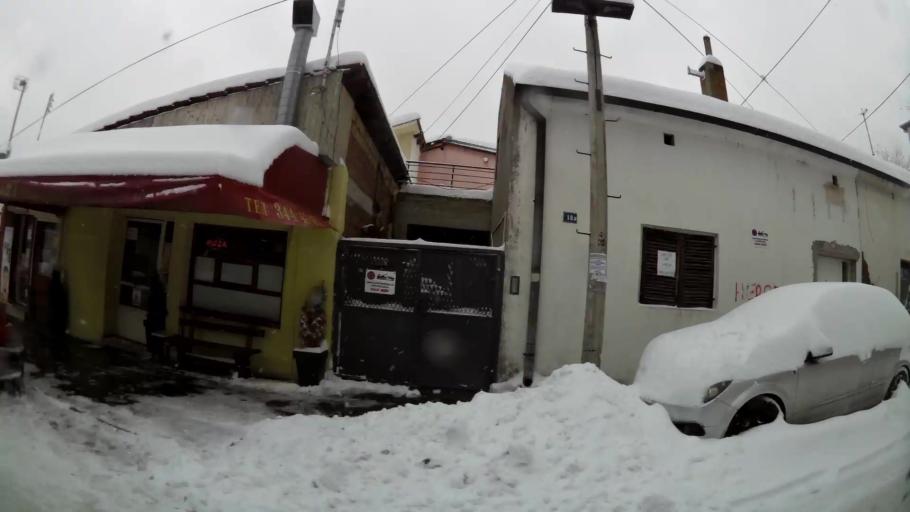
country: RS
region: Central Serbia
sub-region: Belgrade
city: Vracar
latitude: 44.7869
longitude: 20.4845
